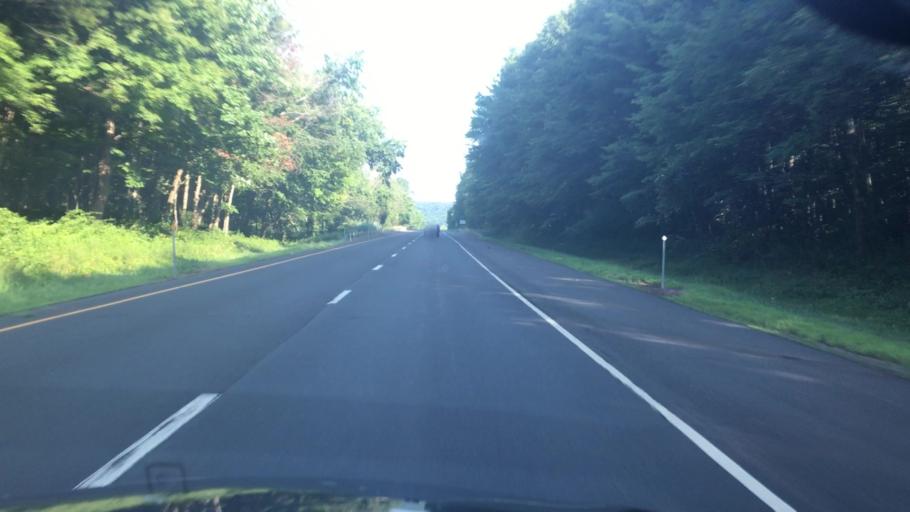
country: US
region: Connecticut
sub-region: Middlesex County
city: Higganum
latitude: 41.5016
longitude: -72.5798
